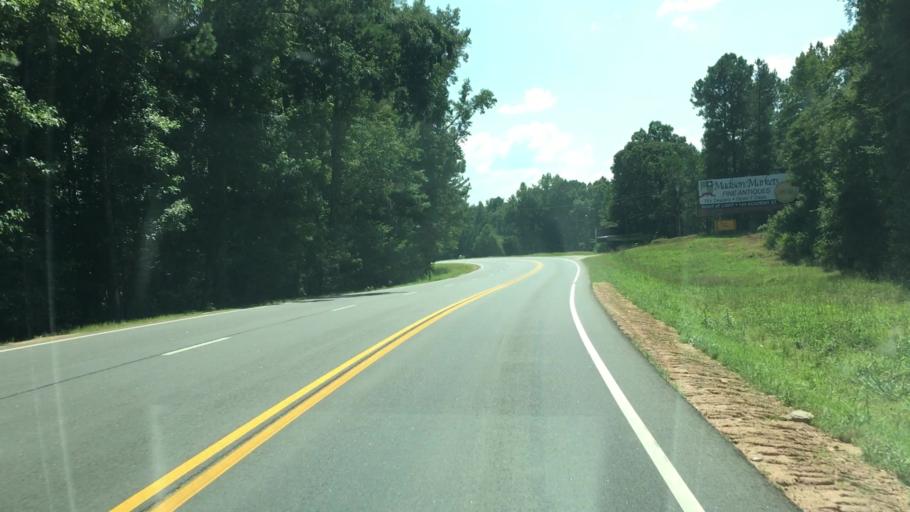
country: US
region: Georgia
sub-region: Morgan County
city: Madison
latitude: 33.7265
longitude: -83.4309
